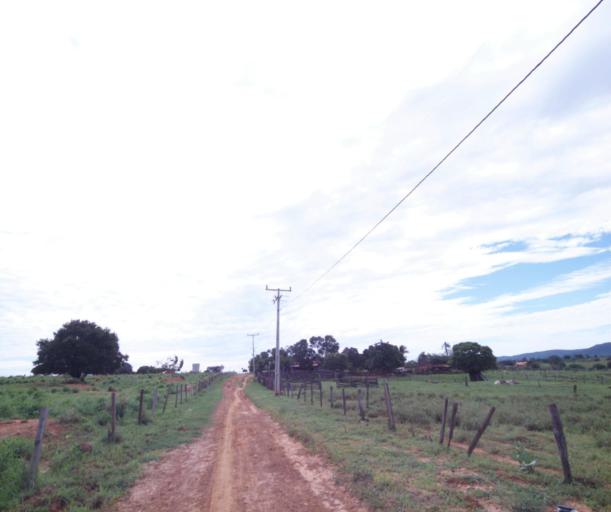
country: BR
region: Bahia
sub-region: Carinhanha
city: Carinhanha
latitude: -14.2406
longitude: -44.3900
